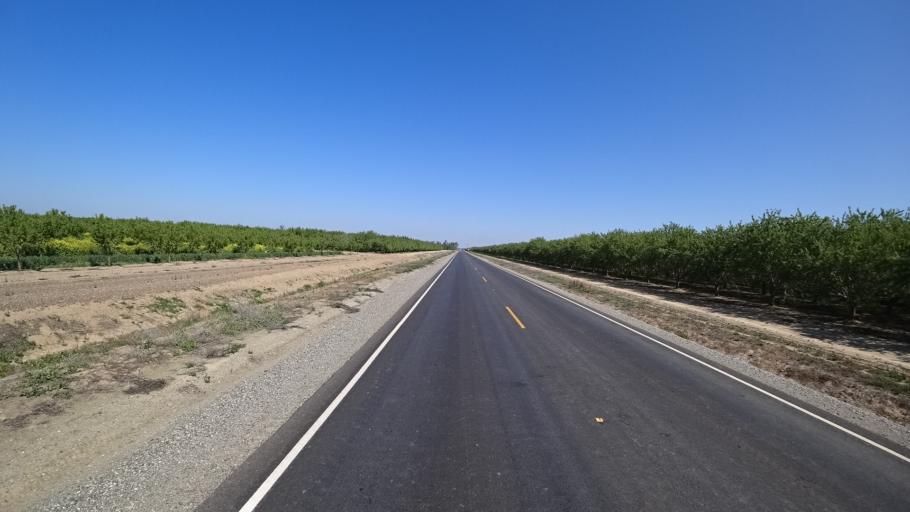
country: US
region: California
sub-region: Glenn County
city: Hamilton City
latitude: 39.6481
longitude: -122.0650
